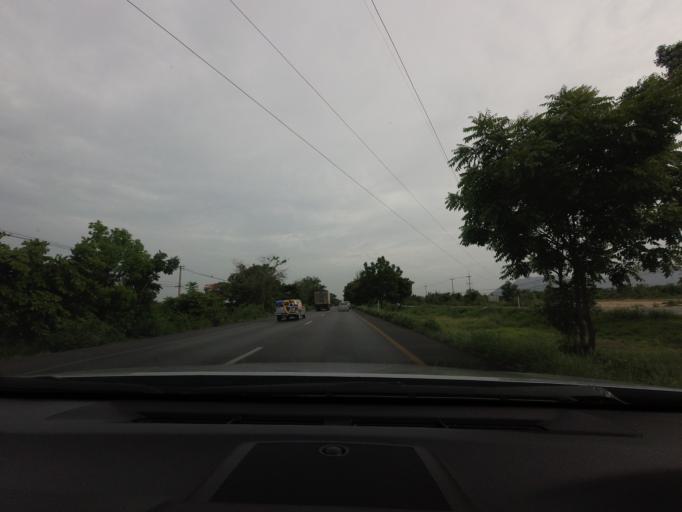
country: TH
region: Phetchaburi
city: Cha-am
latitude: 12.7795
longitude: 99.9375
